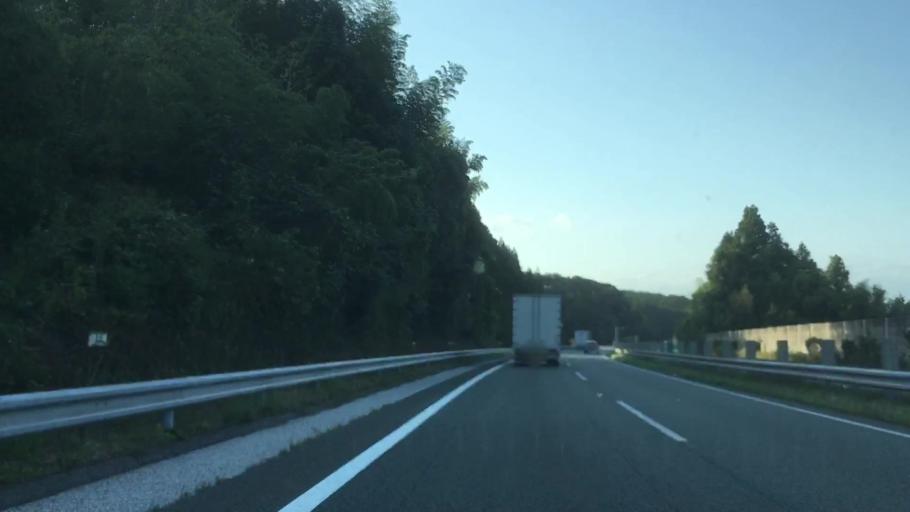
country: JP
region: Yamaguchi
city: Ogori-shimogo
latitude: 34.1450
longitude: 131.3471
